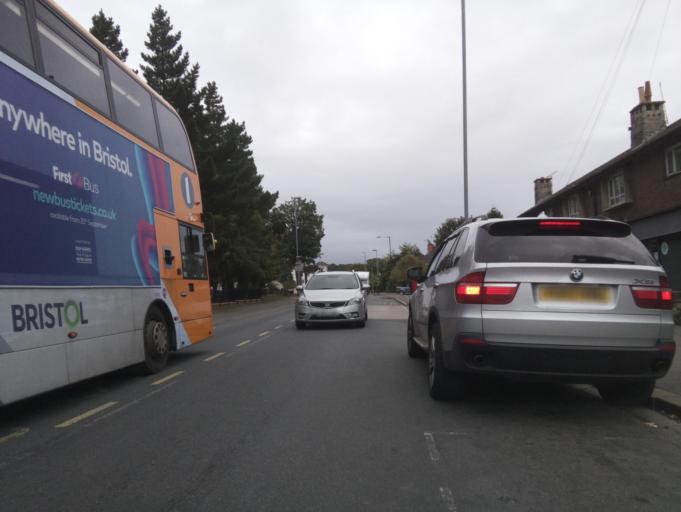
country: GB
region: England
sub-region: South Gloucestershire
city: Severn Beach
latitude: 51.5116
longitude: -2.6294
